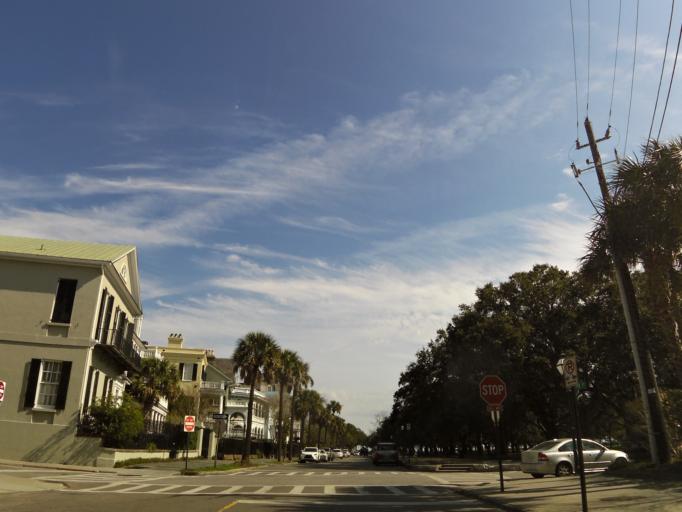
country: US
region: South Carolina
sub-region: Charleston County
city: Charleston
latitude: 32.7705
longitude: -79.9322
